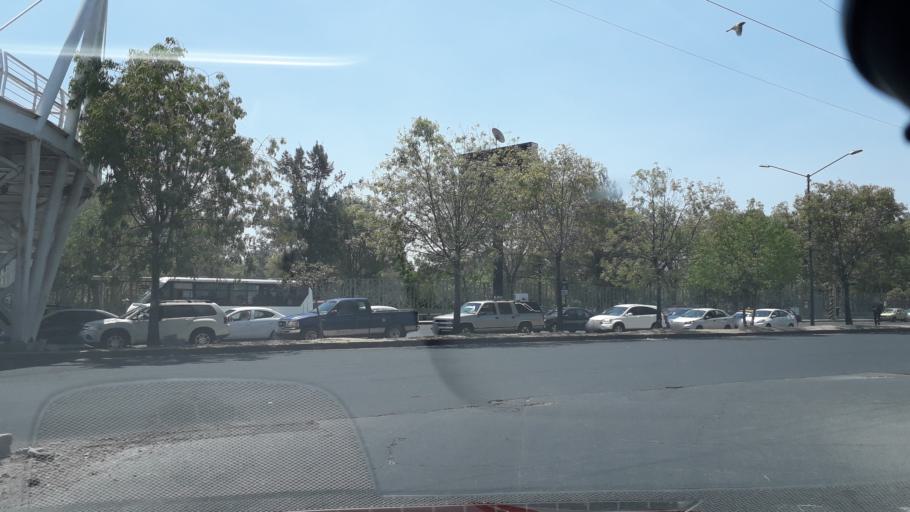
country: MX
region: Puebla
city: Puebla
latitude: 19.0251
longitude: -98.1911
